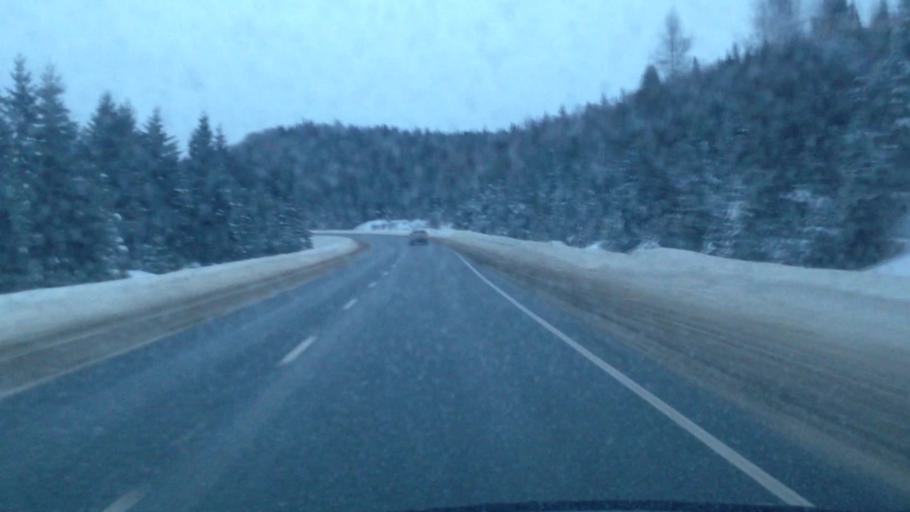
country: CA
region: Quebec
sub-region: Laurentides
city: Sainte-Agathe-des-Monts
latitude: 46.1137
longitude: -74.4275
